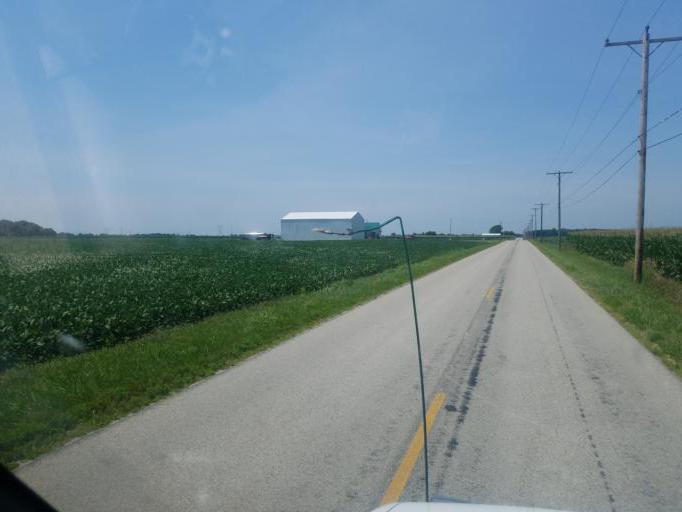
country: US
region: Ohio
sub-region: Shelby County
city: Sidney
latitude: 40.3040
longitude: -84.0737
